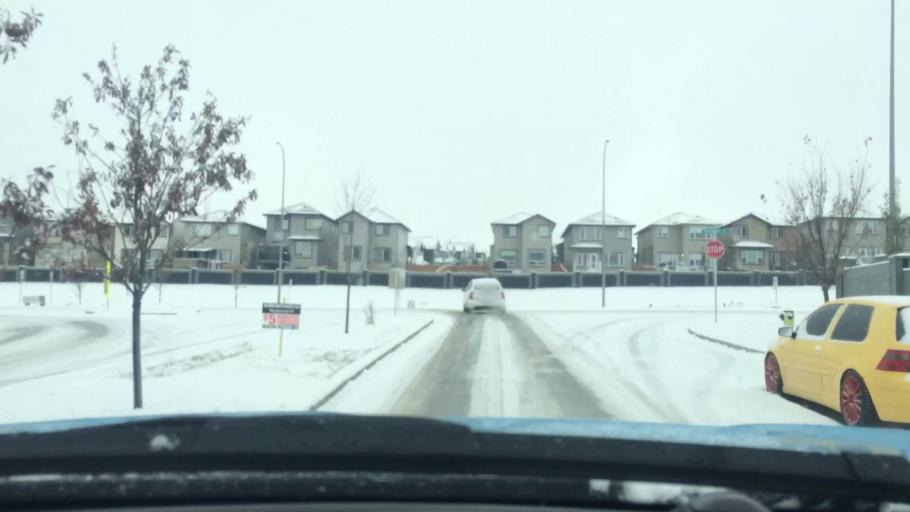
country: CA
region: Alberta
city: Calgary
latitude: 51.1754
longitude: -114.1560
